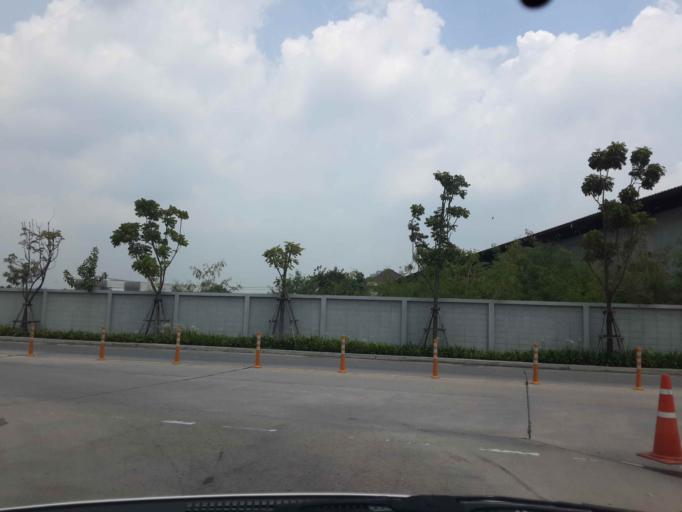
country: TH
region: Bangkok
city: Bang Na
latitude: 13.6484
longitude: 100.6791
